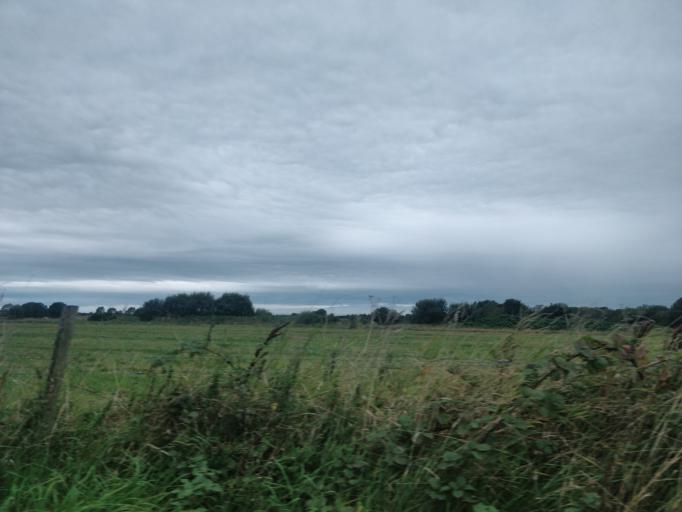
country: GB
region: England
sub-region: Lancashire
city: Ormskirk
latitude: 53.5950
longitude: -2.8627
